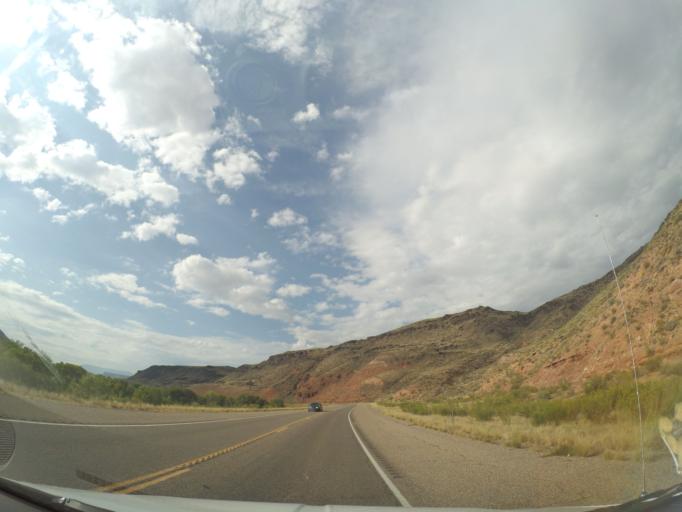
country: US
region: Utah
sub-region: Washington County
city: LaVerkin
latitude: 37.1746
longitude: -113.1142
